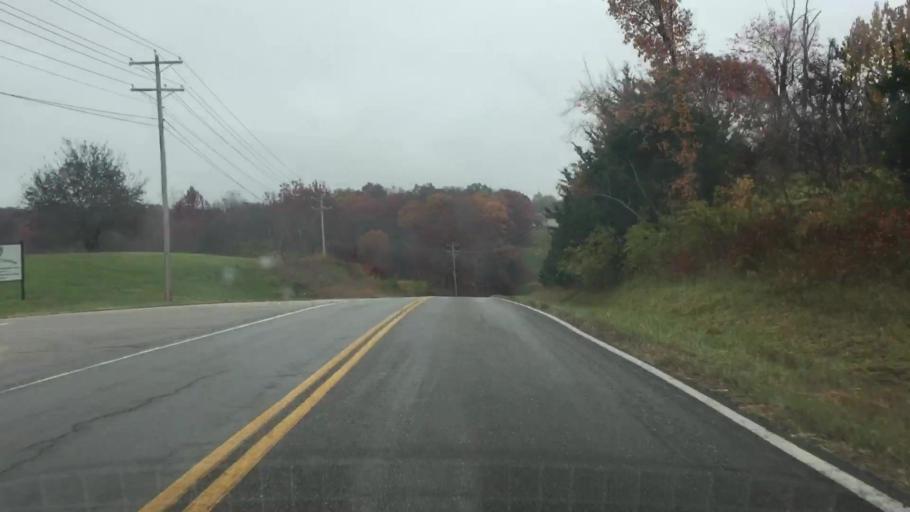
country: US
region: Missouri
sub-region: Callaway County
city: Fulton
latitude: 38.8431
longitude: -91.9277
